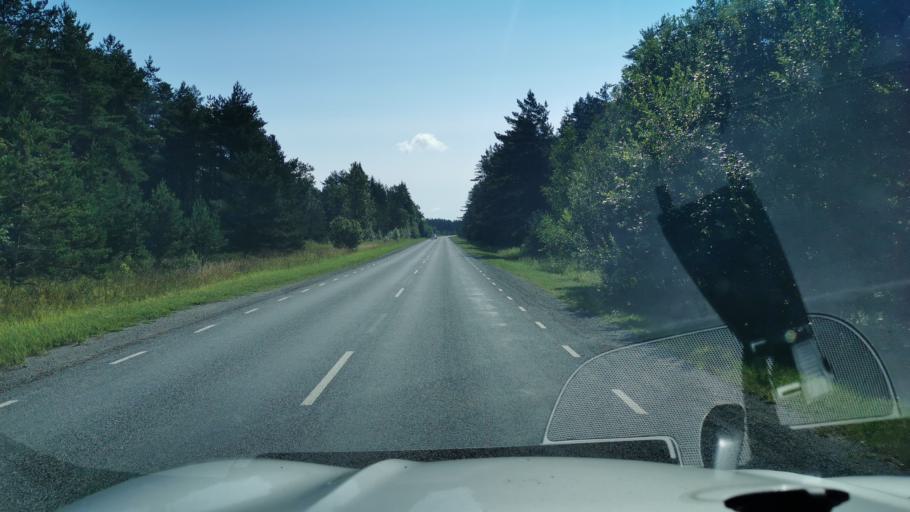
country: EE
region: Harju
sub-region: Paldiski linn
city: Paldiski
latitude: 59.2191
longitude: 24.0821
